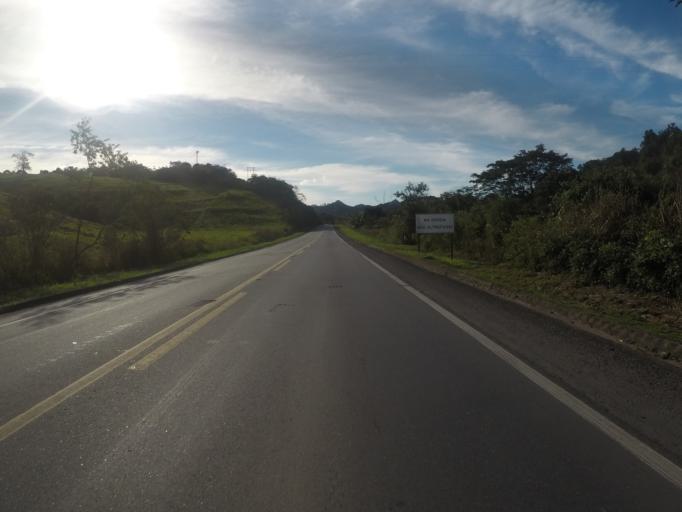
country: BR
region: Espirito Santo
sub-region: Fundao
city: Fundao
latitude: -19.8844
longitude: -40.4156
